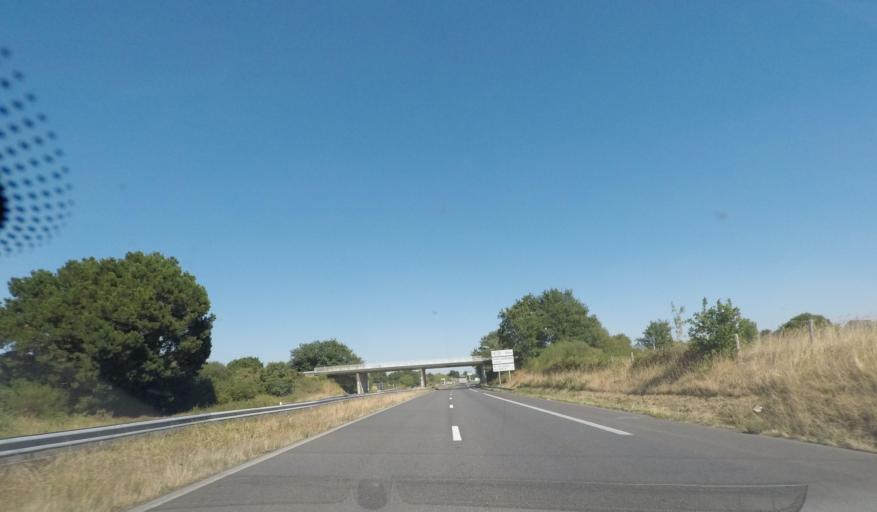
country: FR
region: Pays de la Loire
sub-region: Departement de la Loire-Atlantique
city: Pontchateau
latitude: 47.4481
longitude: -2.1023
